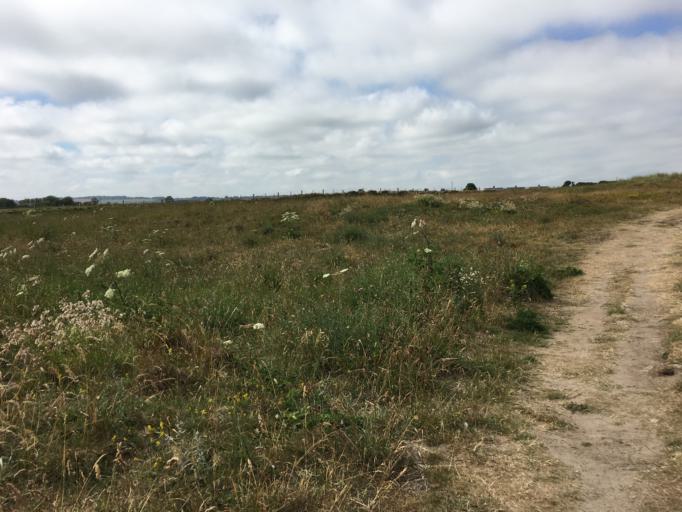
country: GB
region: England
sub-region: Northumberland
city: Alnmouth
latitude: 55.4147
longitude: -1.5816
